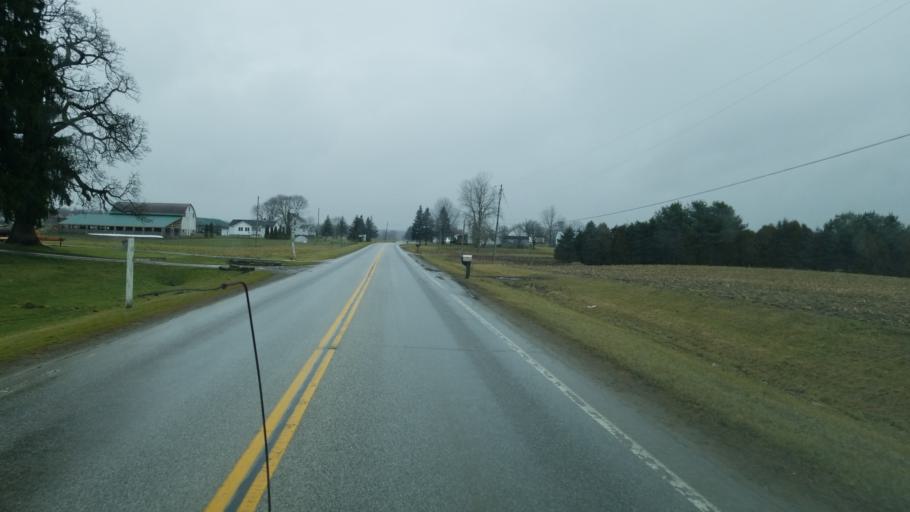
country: US
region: Ohio
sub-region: Geauga County
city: Middlefield
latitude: 41.4243
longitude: -80.9552
